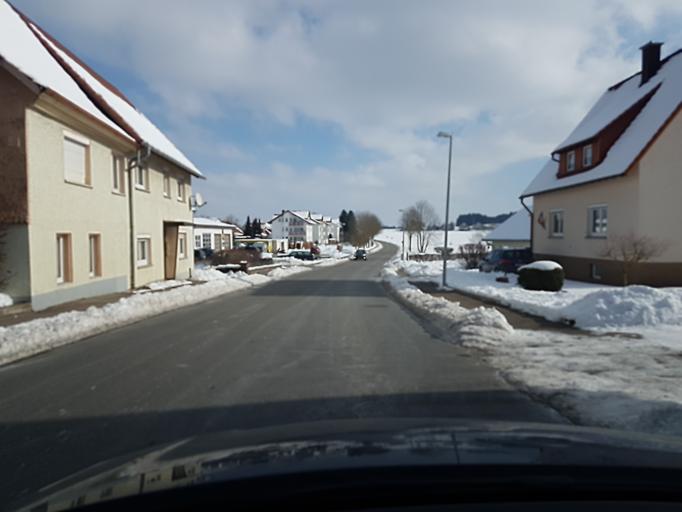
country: DE
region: Baden-Wuerttemberg
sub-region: Freiburg Region
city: Hardt
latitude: 48.1857
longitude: 8.4592
